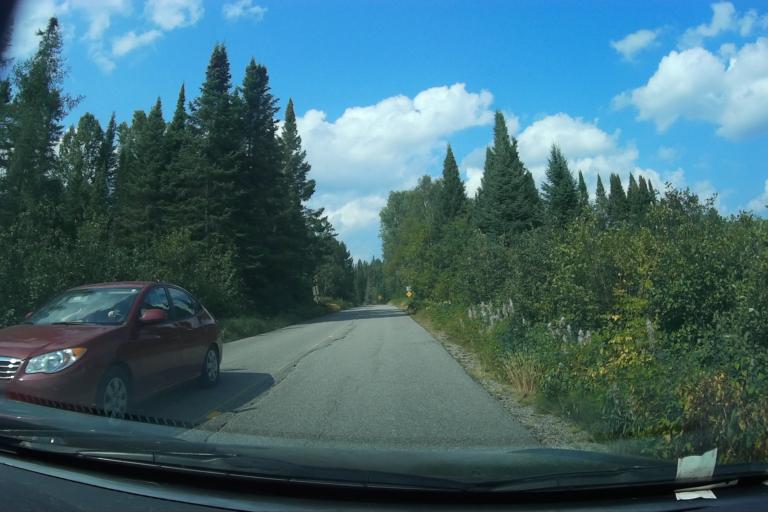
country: CA
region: Ontario
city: Bancroft
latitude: 45.6285
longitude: -78.3516
